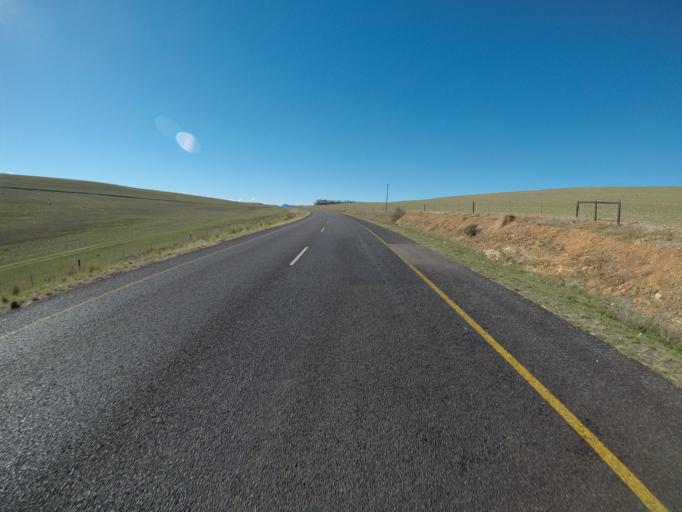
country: ZA
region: Western Cape
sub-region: Overberg District Municipality
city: Caledon
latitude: -34.1448
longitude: 19.4960
